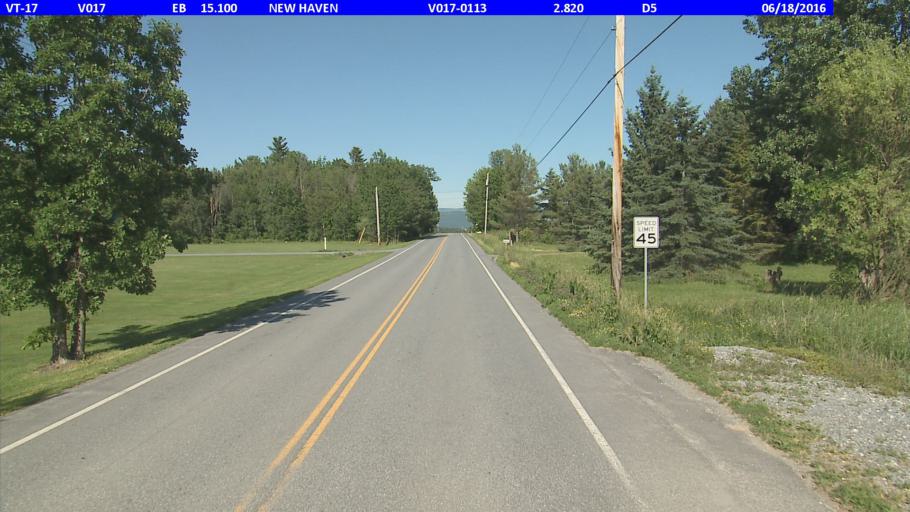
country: US
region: Vermont
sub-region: Addison County
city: Vergennes
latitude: 44.1189
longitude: -73.1942
